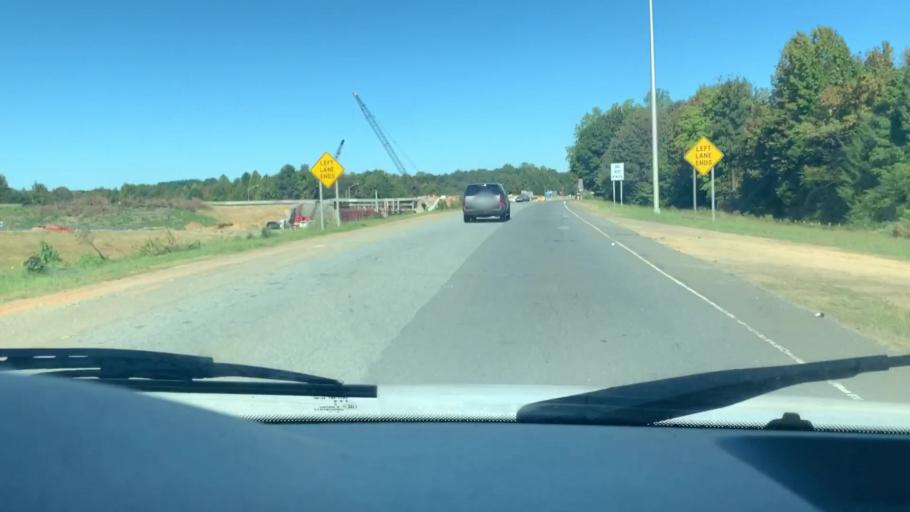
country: US
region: North Carolina
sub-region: Mecklenburg County
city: Charlotte
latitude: 35.2765
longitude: -80.8435
